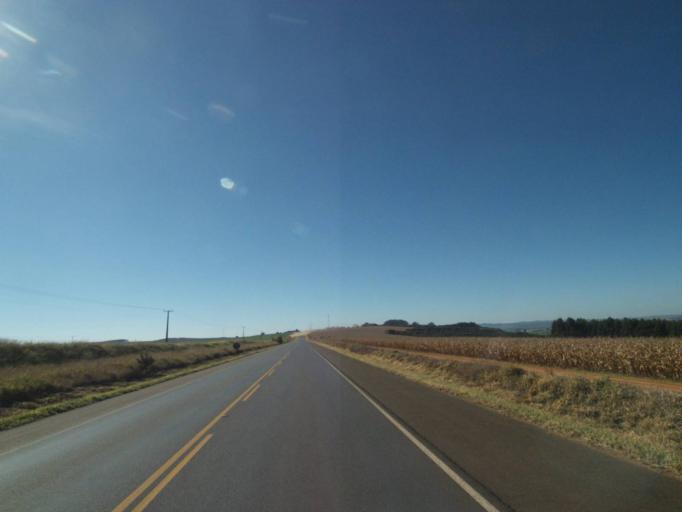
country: BR
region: Parana
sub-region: Tibagi
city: Tibagi
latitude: -24.3548
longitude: -50.3162
